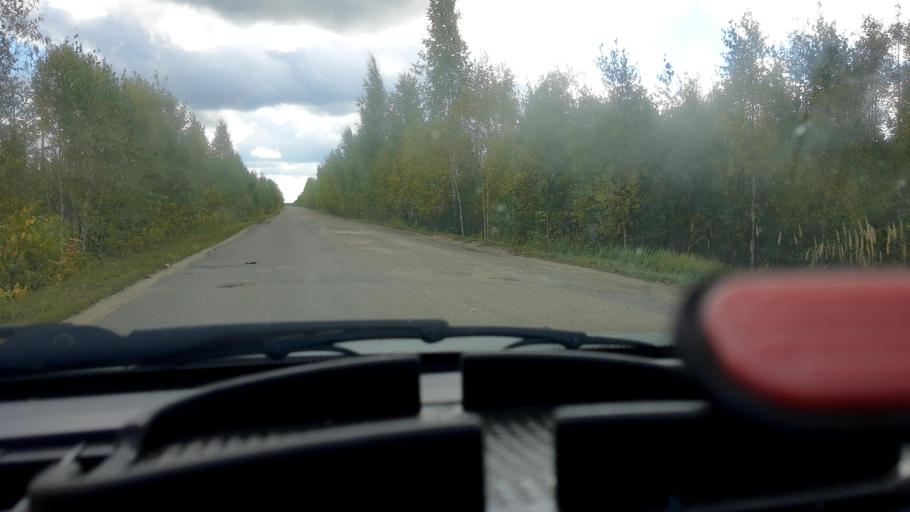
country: RU
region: Mariy-El
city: Kilemary
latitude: 56.9011
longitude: 46.7422
